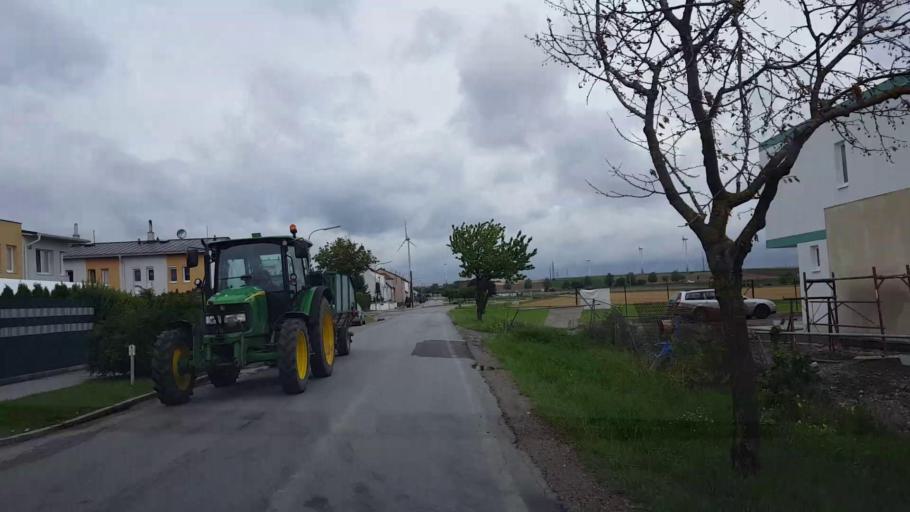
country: AT
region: Lower Austria
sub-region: Politischer Bezirk Bruck an der Leitha
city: Bruck an der Leitha
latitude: 48.0186
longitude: 16.7201
